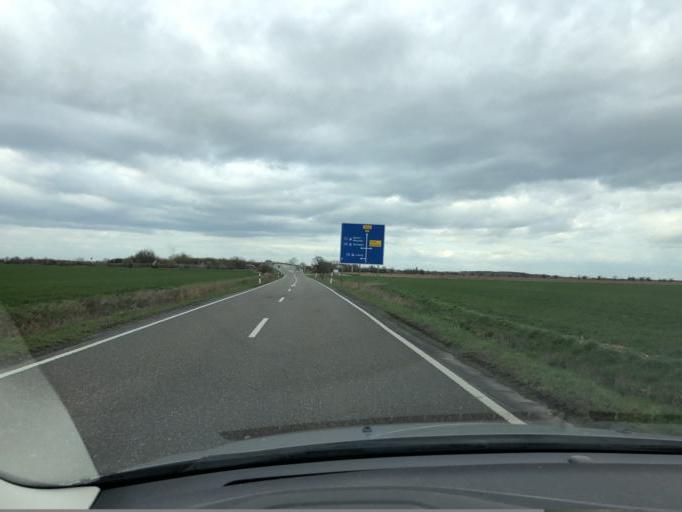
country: DE
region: Saxony-Anhalt
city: Lutzen
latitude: 51.2344
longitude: 12.1389
